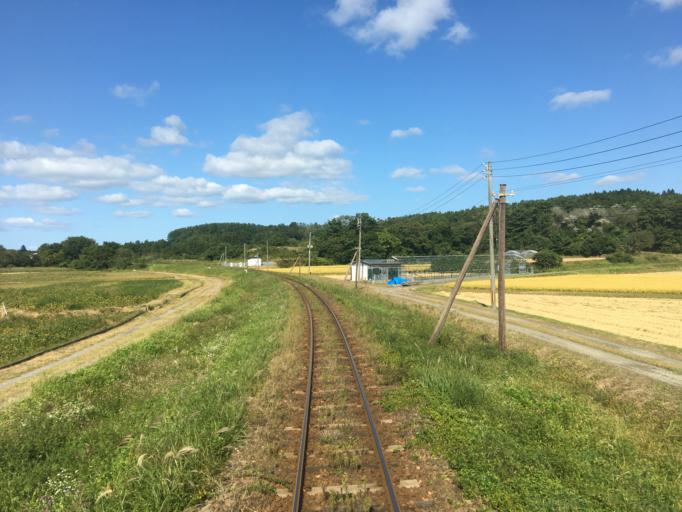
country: JP
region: Aomori
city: Goshogawara
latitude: 40.9524
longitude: 140.4424
